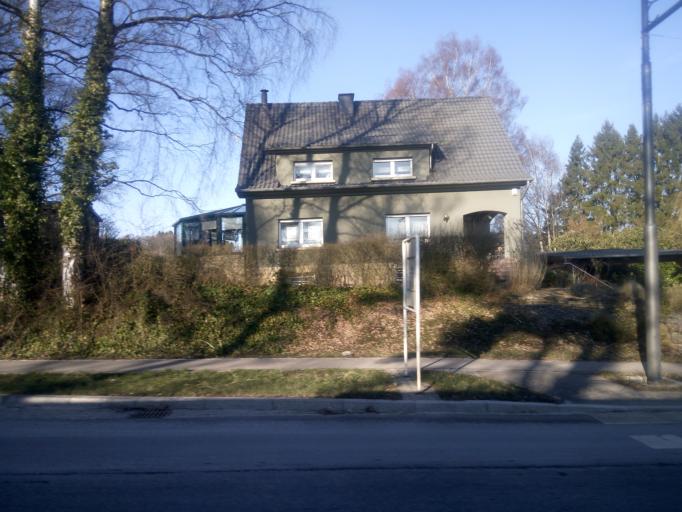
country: LU
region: Grevenmacher
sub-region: Canton de Grevenmacher
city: Junglinster
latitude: 49.7035
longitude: 6.2480
